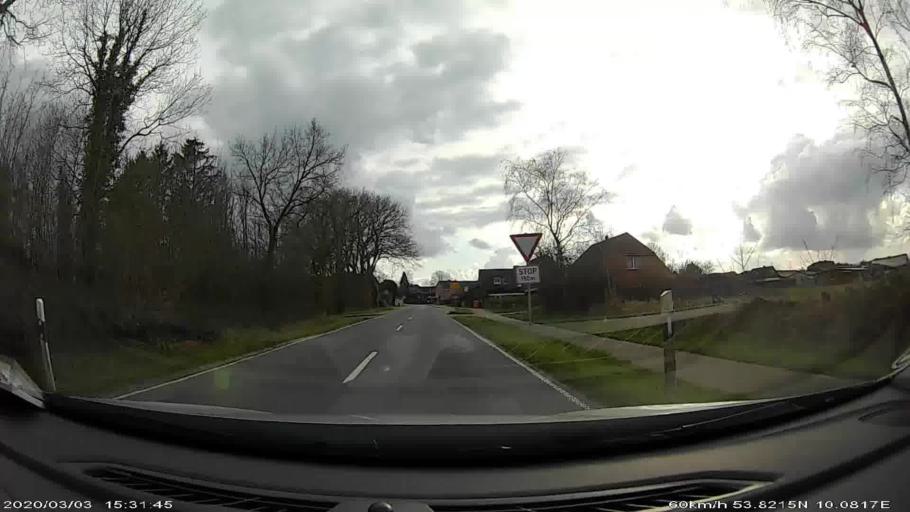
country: DE
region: Schleswig-Holstein
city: Huttblek
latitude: 53.8224
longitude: 10.0823
